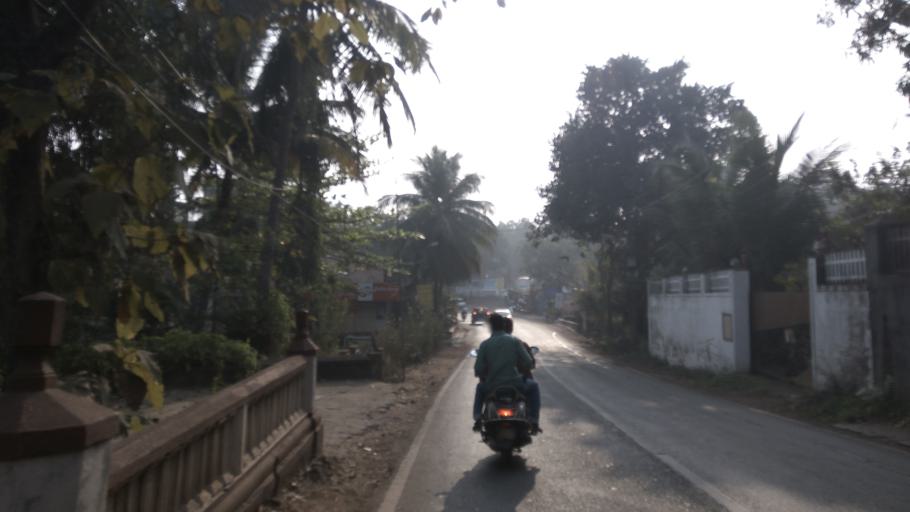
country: IN
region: Goa
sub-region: North Goa
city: Saligao
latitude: 15.5433
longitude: 73.8100
